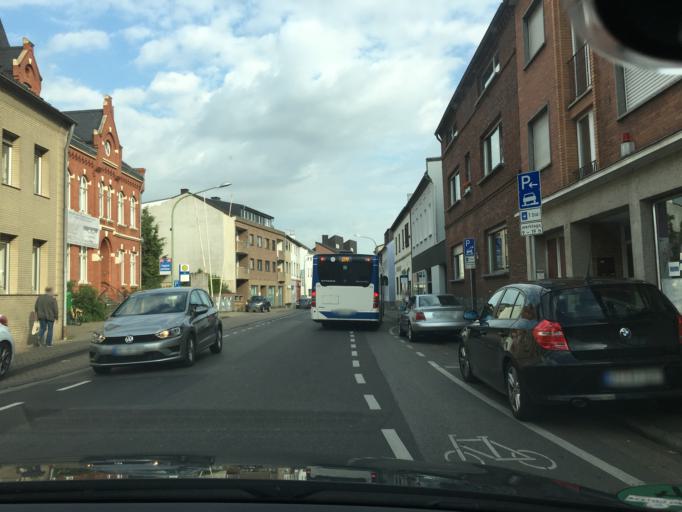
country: DE
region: North Rhine-Westphalia
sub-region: Regierungsbezirk Koln
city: Dueren
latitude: 50.8210
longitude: 6.4638
